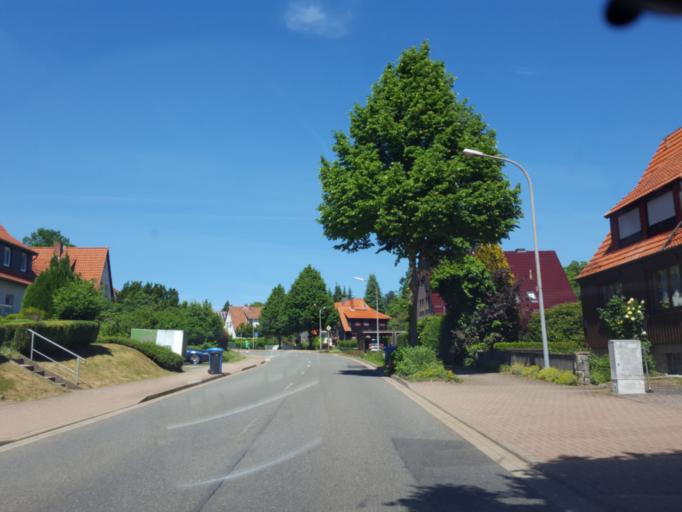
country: DE
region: Lower Saxony
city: Osterode am Harz
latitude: 51.7145
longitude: 10.2583
